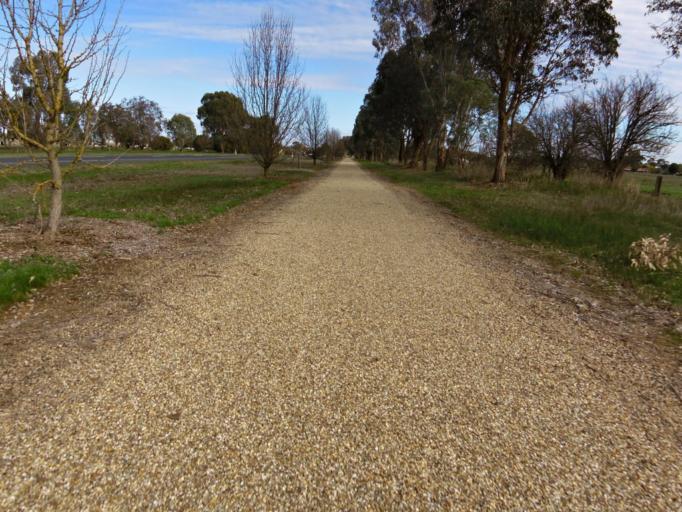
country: AU
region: Victoria
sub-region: Wangaratta
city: Wangaratta
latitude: -36.4504
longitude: 146.4399
